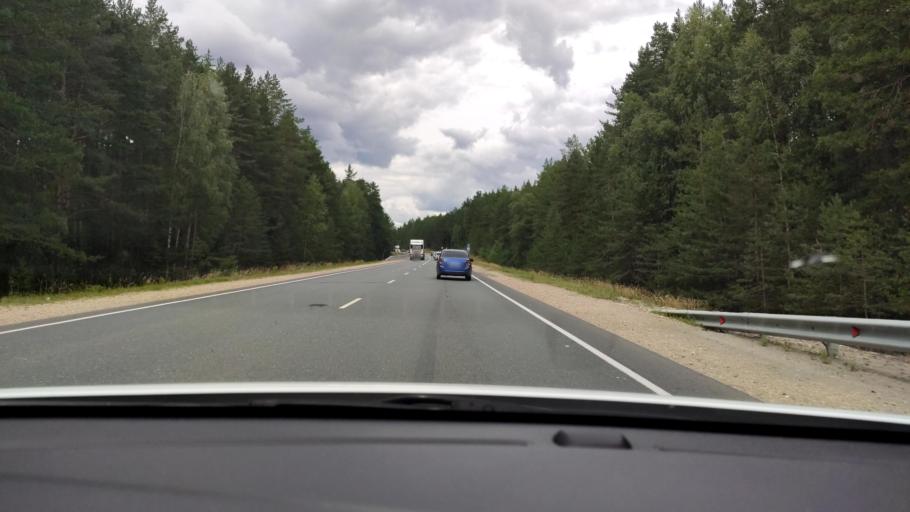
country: RU
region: Mariy-El
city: Pomary
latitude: 56.0572
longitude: 48.3720
